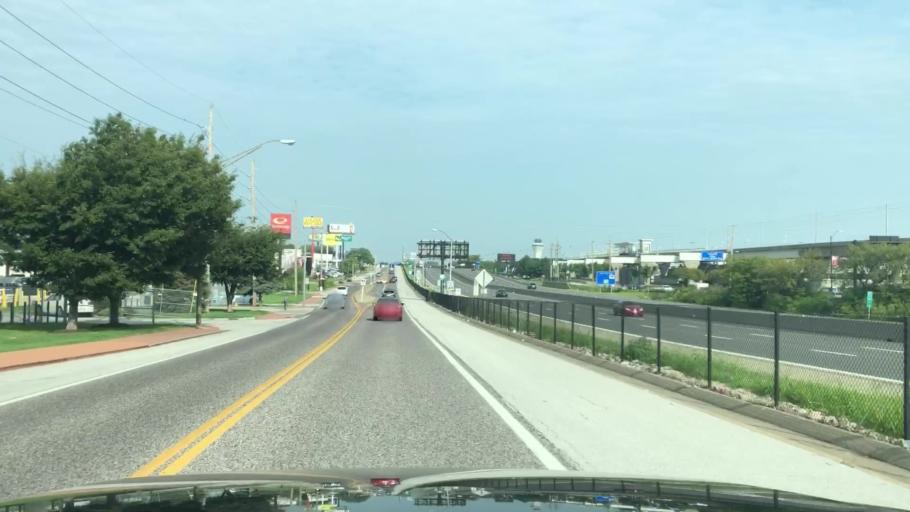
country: US
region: Missouri
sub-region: Saint Louis County
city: Woodson Terrace
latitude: 38.7342
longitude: -90.3541
